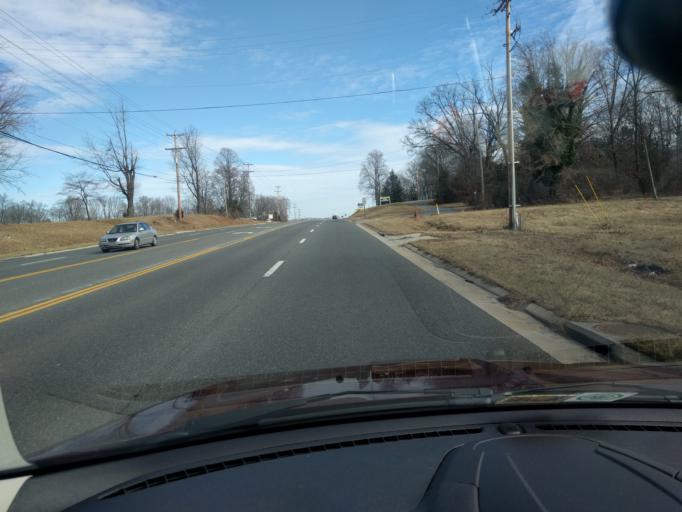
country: US
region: Virginia
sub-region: Bedford County
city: Forest
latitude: 37.3651
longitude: -79.2683
